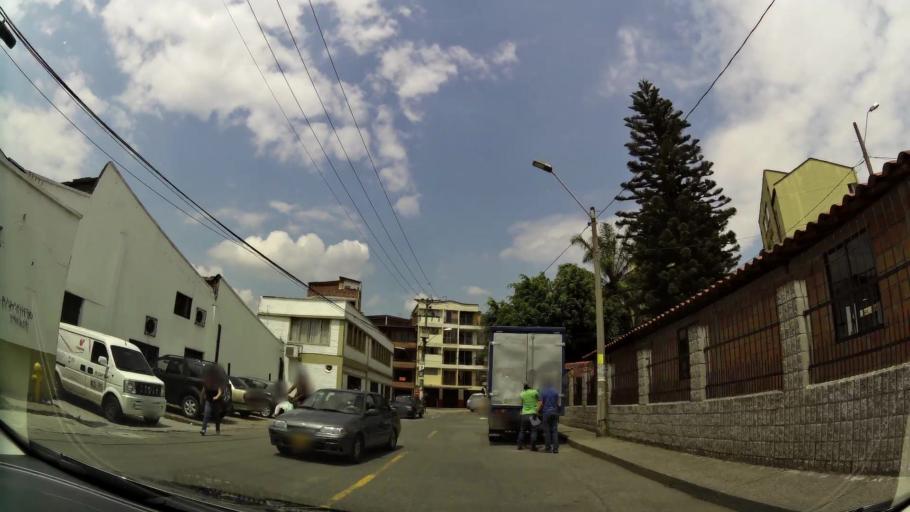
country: CO
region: Antioquia
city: Itagui
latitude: 6.1904
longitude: -75.5958
